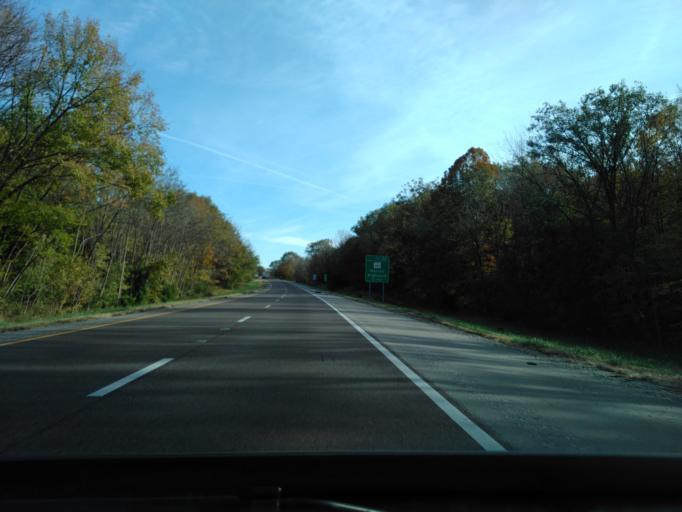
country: US
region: Illinois
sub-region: Madison County
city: Saint Jacob
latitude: 38.7682
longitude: -89.7538
